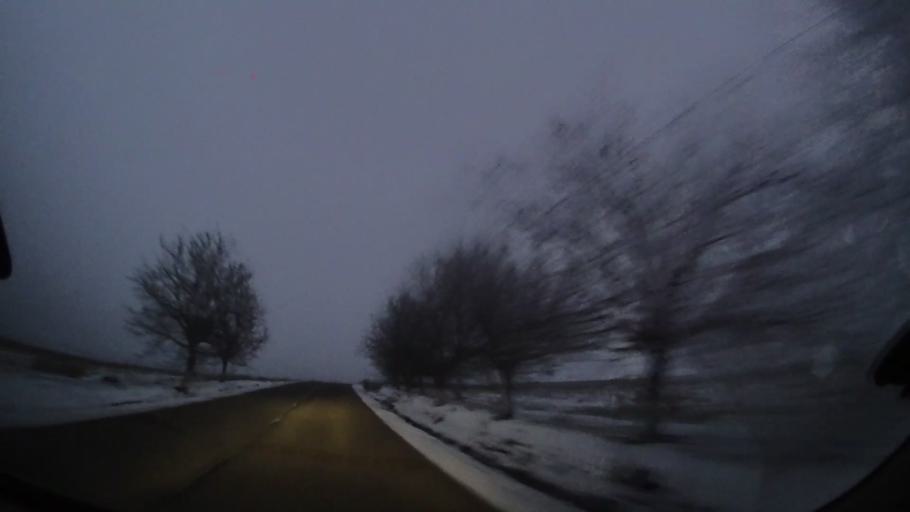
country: RO
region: Vaslui
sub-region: Comuna Hoceni
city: Hoceni
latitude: 46.5222
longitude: 28.0258
